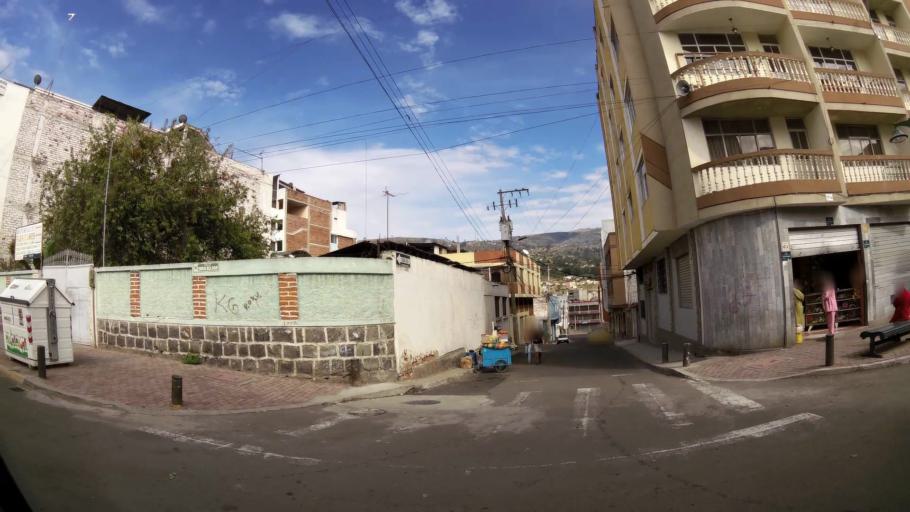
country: EC
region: Tungurahua
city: Ambato
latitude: -1.2414
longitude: -78.6354
